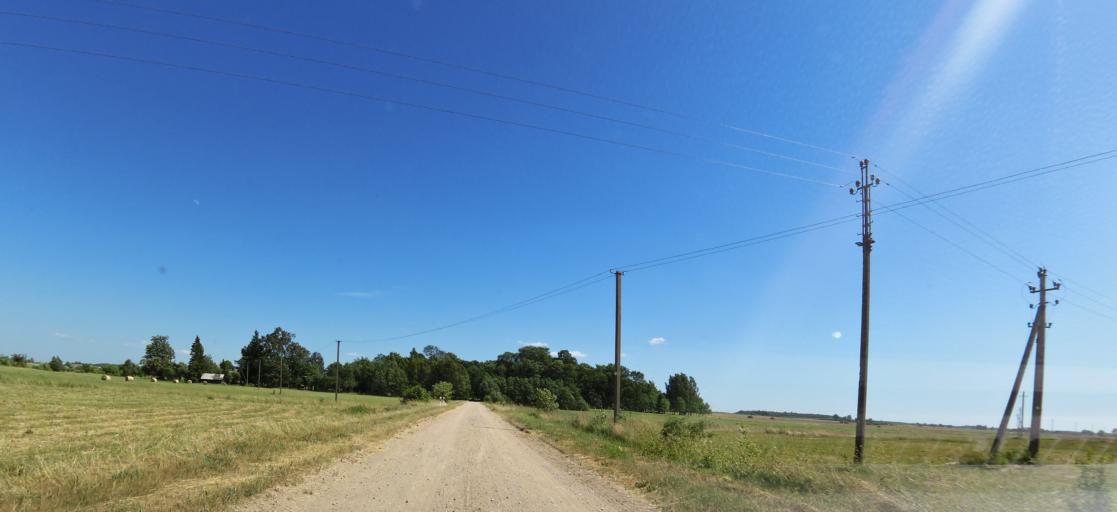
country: LT
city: Vabalninkas
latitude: 55.9817
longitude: 24.7576
